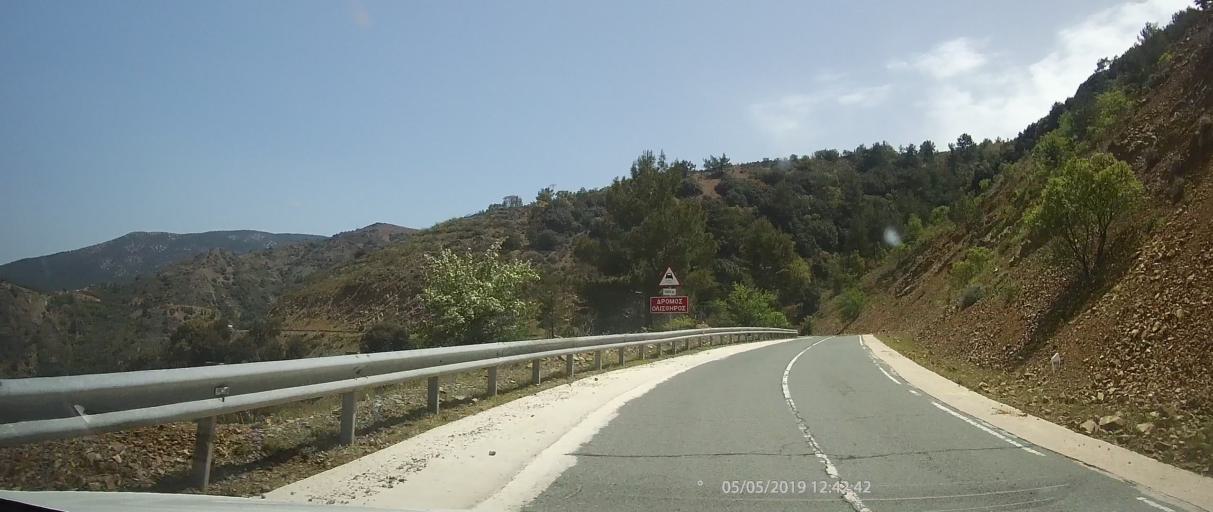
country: CY
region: Lefkosia
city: Kakopetria
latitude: 34.9720
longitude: 32.8119
